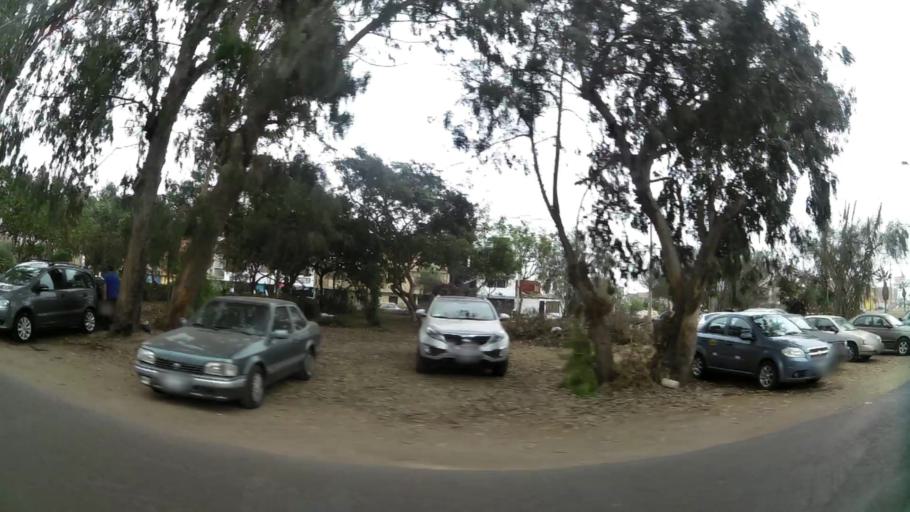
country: PE
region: Lima
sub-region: Lima
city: Surco
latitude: -12.1584
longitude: -76.9802
